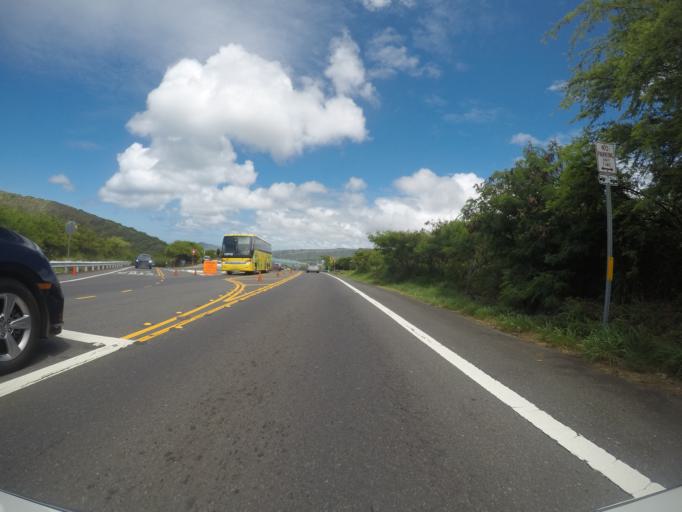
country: US
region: Hawaii
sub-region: Honolulu County
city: Waimanalo Beach
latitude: 21.2752
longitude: -157.6927
